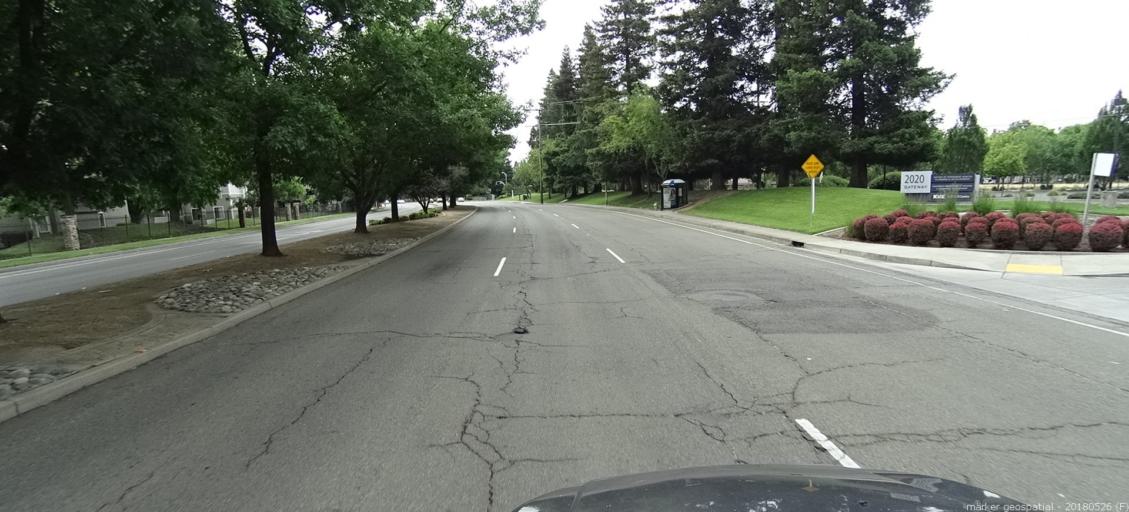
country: US
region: California
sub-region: Sacramento County
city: Sacramento
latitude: 38.6133
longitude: -121.5075
